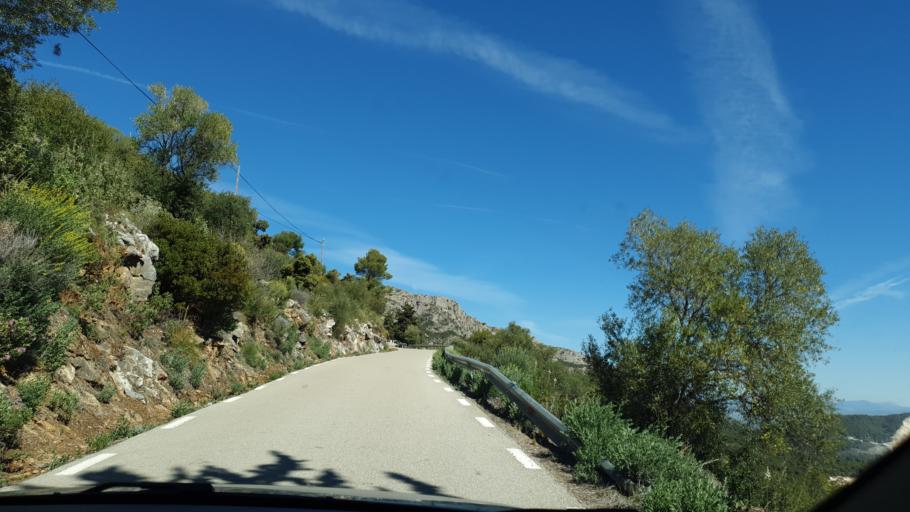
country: ES
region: Andalusia
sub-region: Provincia de Malaga
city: Ojen
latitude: 36.5895
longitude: -4.8718
